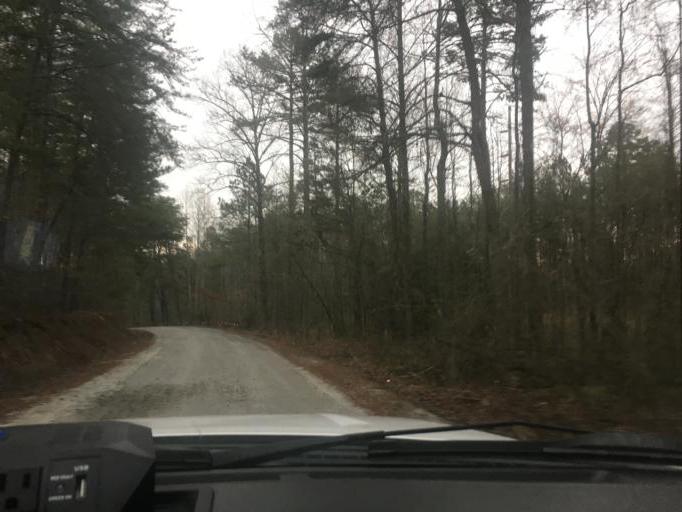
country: US
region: Georgia
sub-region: Dawson County
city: Dawsonville
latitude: 34.4415
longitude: -84.2116
